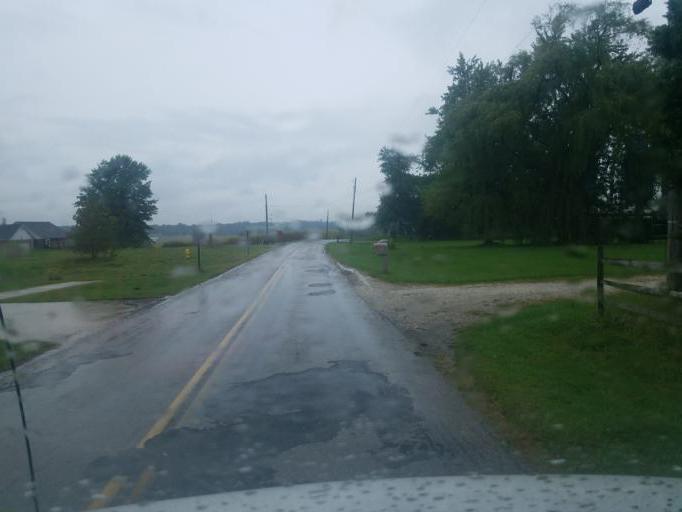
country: US
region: Ohio
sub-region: Wayne County
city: Rittman
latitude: 40.9837
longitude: -81.8024
